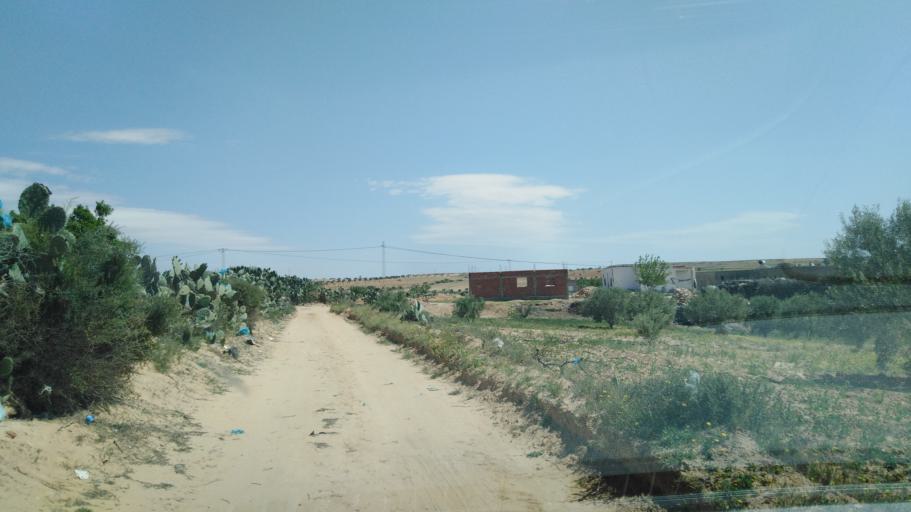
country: TN
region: Safaqis
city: Sfax
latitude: 34.7786
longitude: 10.5247
